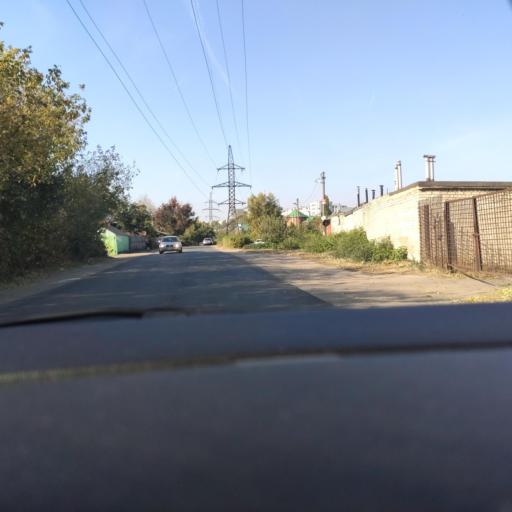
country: RU
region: Voronezj
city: Voronezh
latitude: 51.6885
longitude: 39.2057
